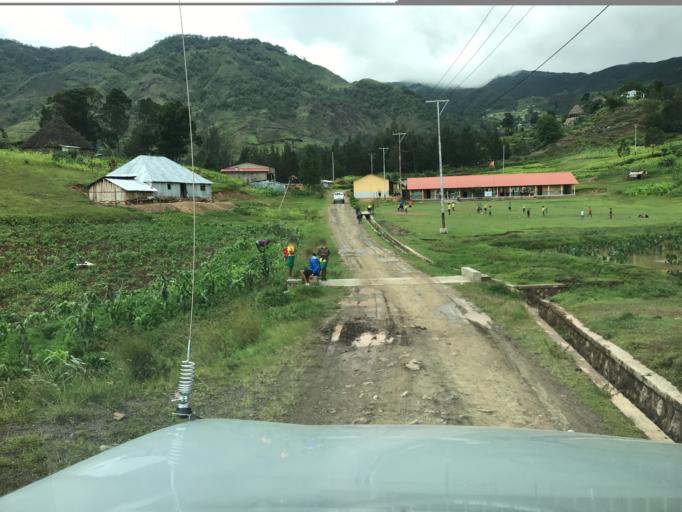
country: TL
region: Aileu
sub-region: Aileu Villa
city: Aileu
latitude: -8.8610
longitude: 125.5713
